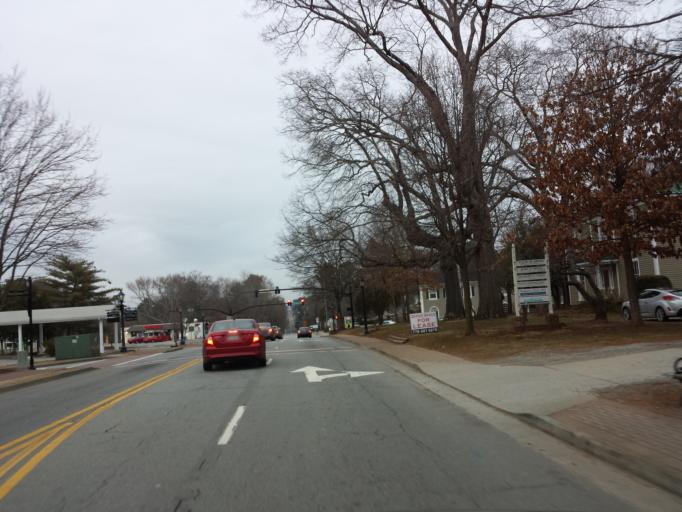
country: US
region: Georgia
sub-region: Fulton County
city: Roswell
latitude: 34.0304
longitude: -84.3614
